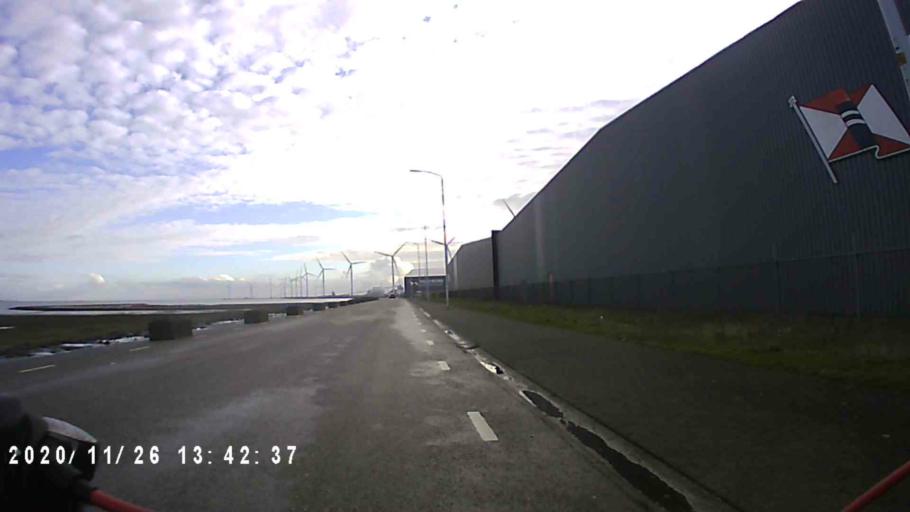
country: NL
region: Groningen
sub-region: Gemeente Delfzijl
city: Delfzijl
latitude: 53.3307
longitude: 6.9401
